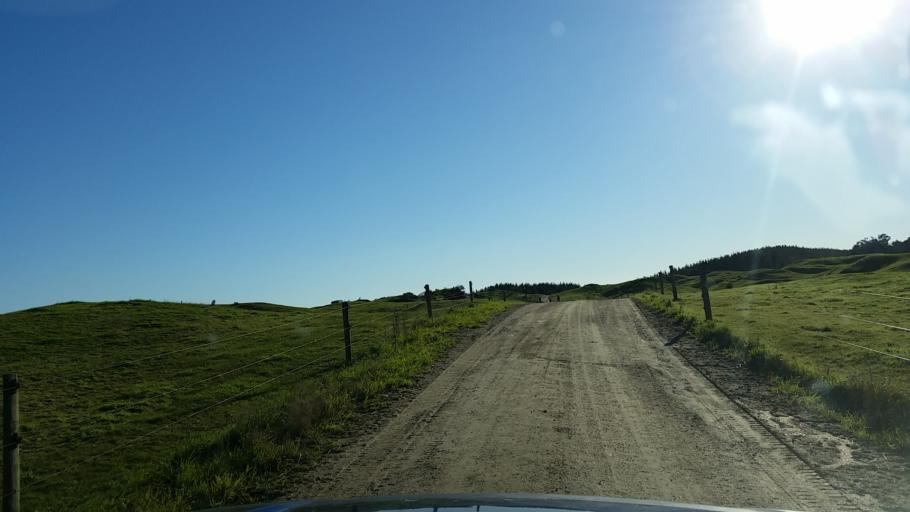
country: NZ
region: Taranaki
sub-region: South Taranaki District
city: Patea
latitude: -39.8370
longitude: 174.6905
